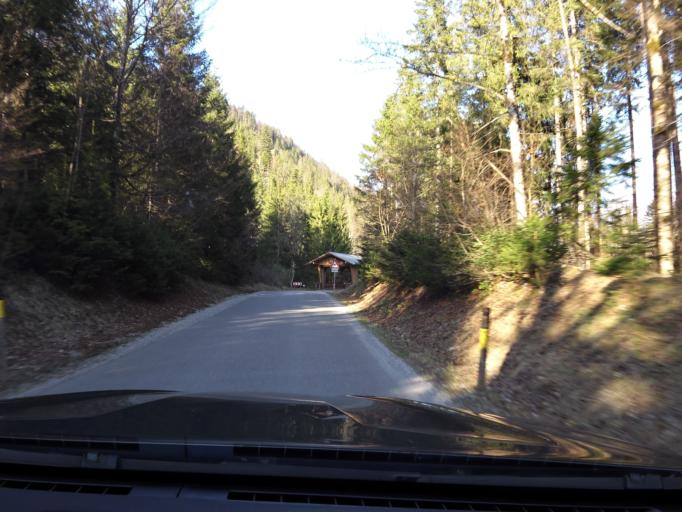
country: DE
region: Bavaria
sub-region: Upper Bavaria
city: Wallgau
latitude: 47.5378
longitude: 11.3344
